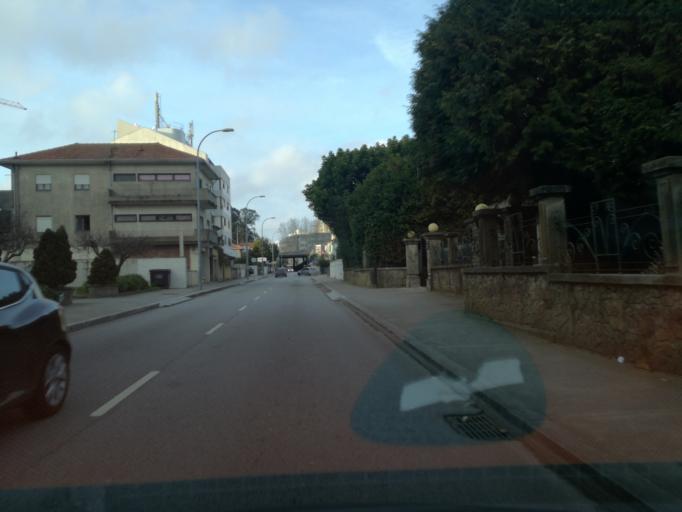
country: PT
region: Porto
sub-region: Porto
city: Porto
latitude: 41.1709
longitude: -8.6259
